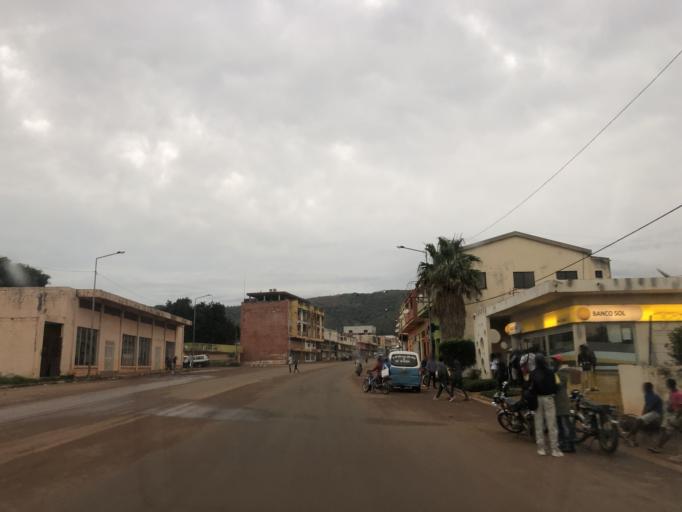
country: AO
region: Cuanza Sul
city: Uacu Cungo
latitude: -11.3571
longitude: 15.1215
